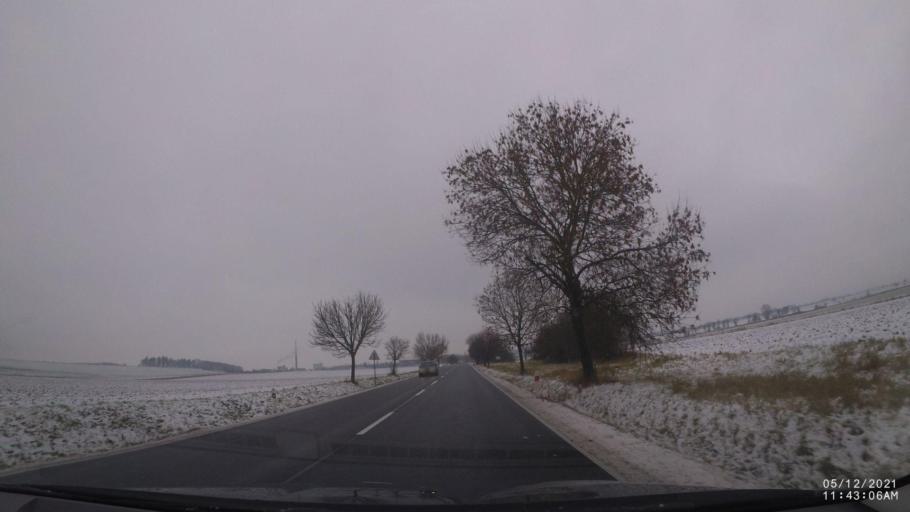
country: CZ
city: Dobruska
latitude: 50.2835
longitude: 16.1763
